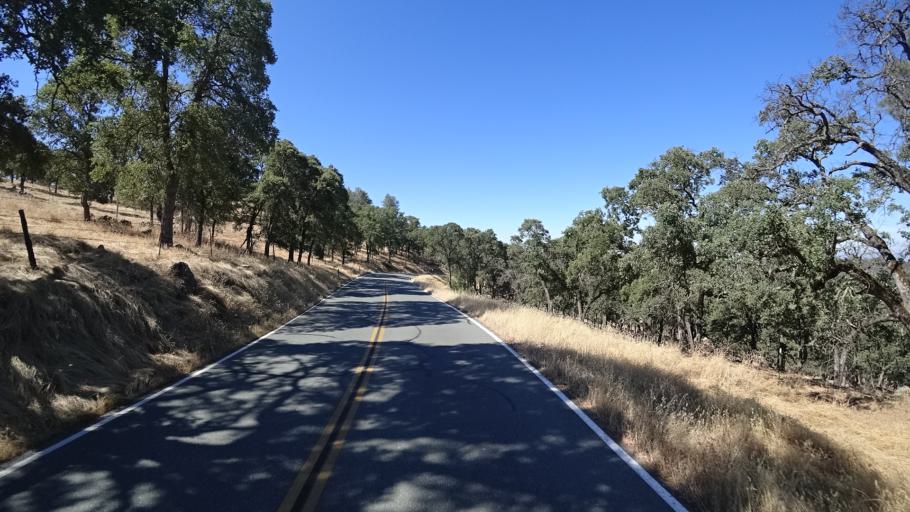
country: US
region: California
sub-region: Calaveras County
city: Valley Springs
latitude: 38.2499
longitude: -120.7781
